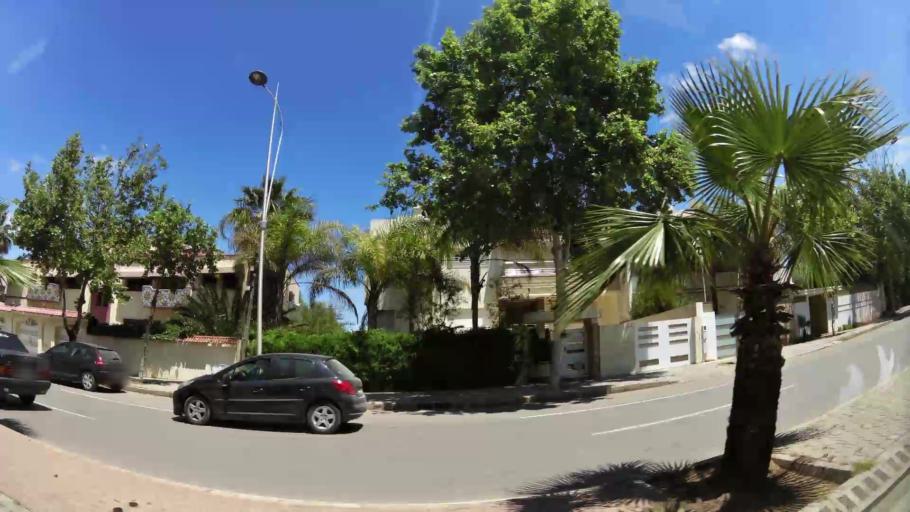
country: MA
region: Fes-Boulemane
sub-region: Fes
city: Fes
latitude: 34.0069
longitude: -4.9941
